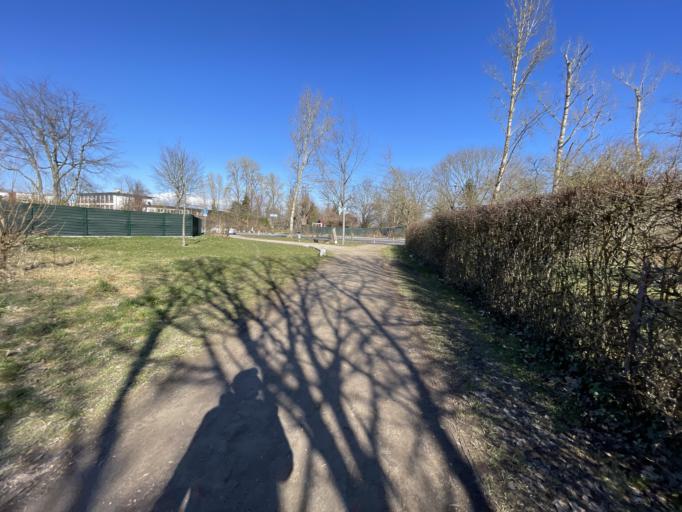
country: DE
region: Hesse
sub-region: Regierungsbezirk Darmstadt
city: Offenbach
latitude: 50.0847
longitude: 8.7646
